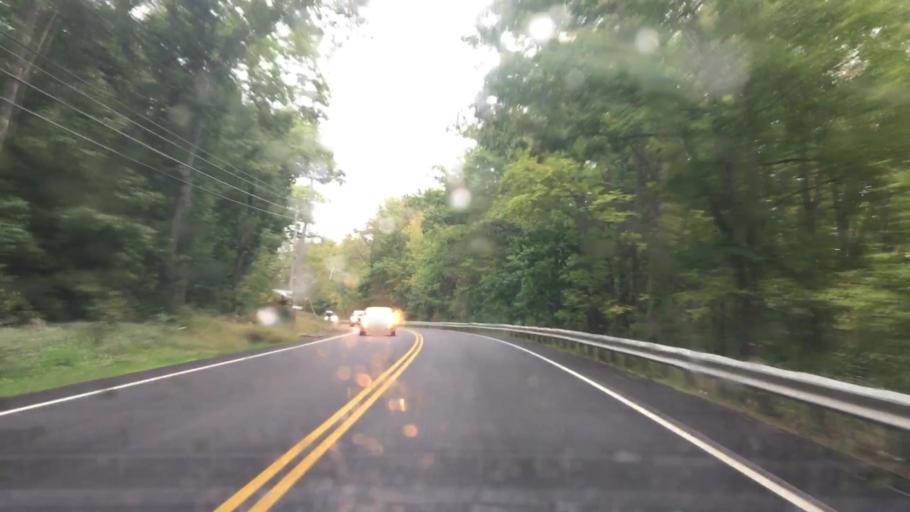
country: US
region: Maine
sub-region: Penobscot County
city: Orrington
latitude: 44.6799
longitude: -68.8077
